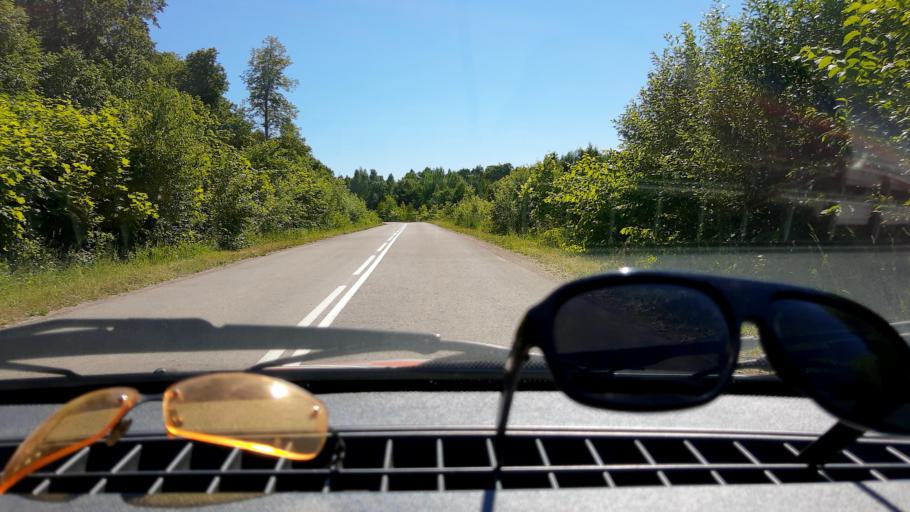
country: RU
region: Bashkortostan
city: Ulu-Telyak
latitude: 54.8224
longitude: 57.0358
